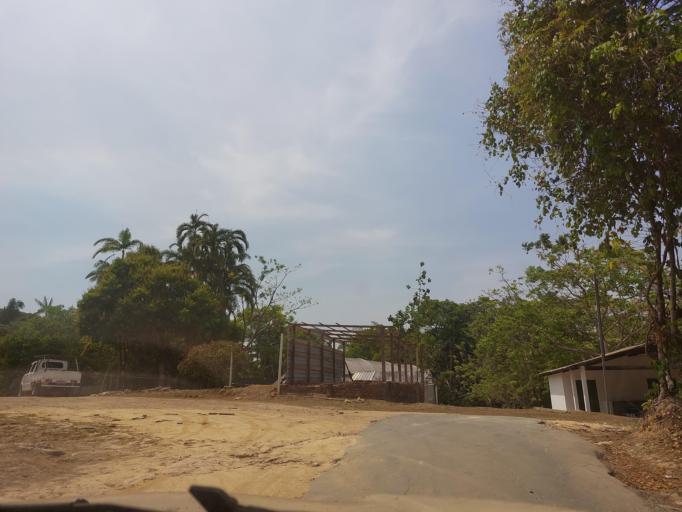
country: BR
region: Amazonas
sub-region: Manaus
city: Manaus
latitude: -3.1008
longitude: -59.9771
